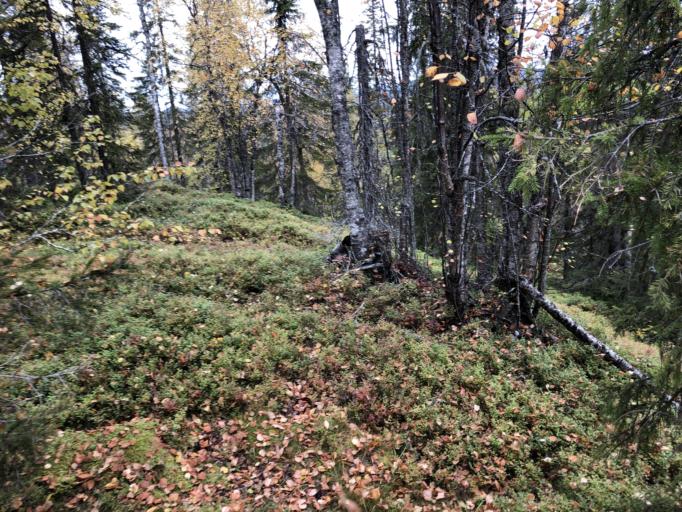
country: FI
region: Northern Ostrobothnia
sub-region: Koillismaa
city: Kuusamo
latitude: 66.5989
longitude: 29.3262
